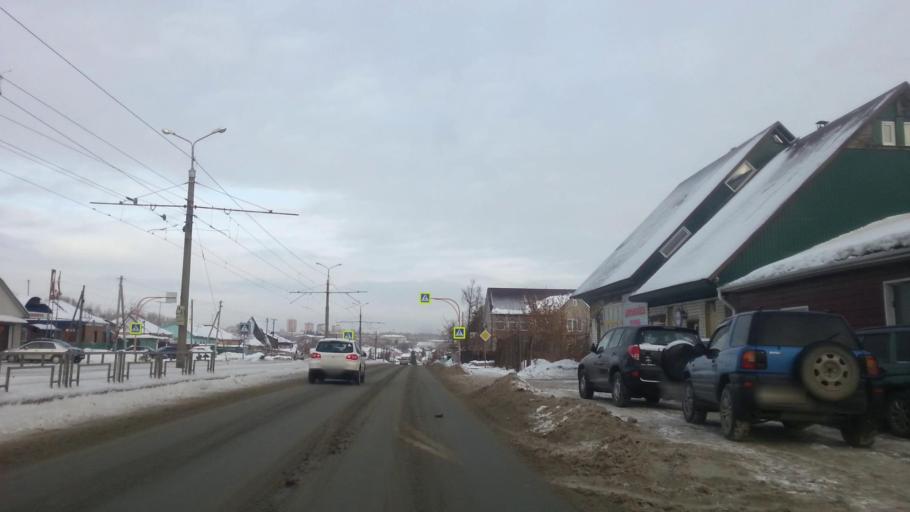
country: RU
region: Altai Krai
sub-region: Gorod Barnaulskiy
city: Barnaul
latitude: 53.3634
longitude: 83.7292
